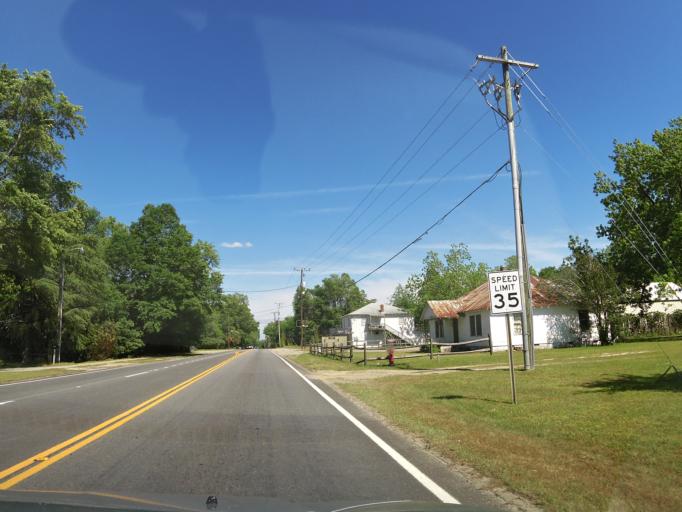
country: US
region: South Carolina
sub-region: Barnwell County
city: Williston
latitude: 33.4034
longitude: -81.4333
